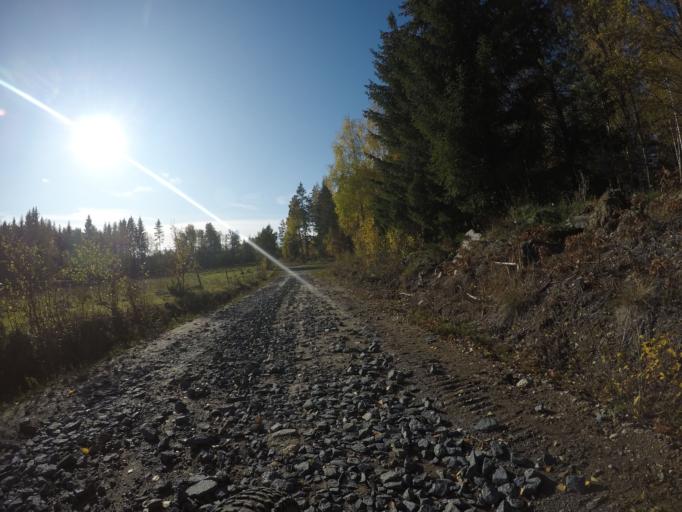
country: SE
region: Vaestmanland
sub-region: Kungsors Kommun
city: Kungsoer
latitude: 59.3225
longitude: 16.0903
